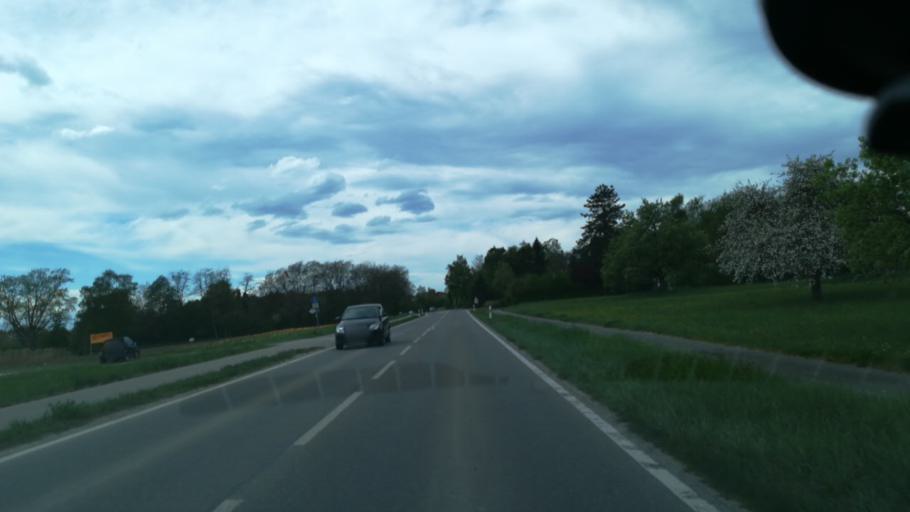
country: DE
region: Baden-Wuerttemberg
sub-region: Freiburg Region
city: Radolfzell am Bodensee
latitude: 47.7467
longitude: 8.9938
